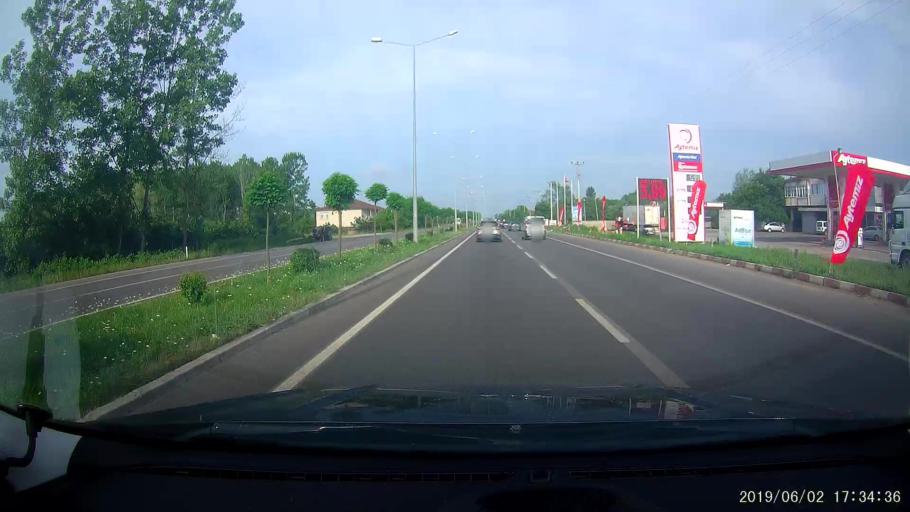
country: TR
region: Samsun
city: Terme
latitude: 41.2201
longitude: 36.8717
